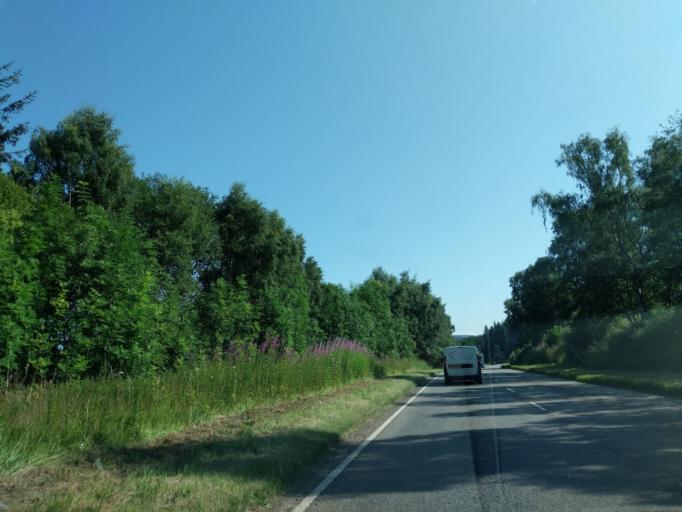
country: GB
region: Scotland
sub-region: Moray
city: Rothes
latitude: 57.5024
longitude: -3.1932
